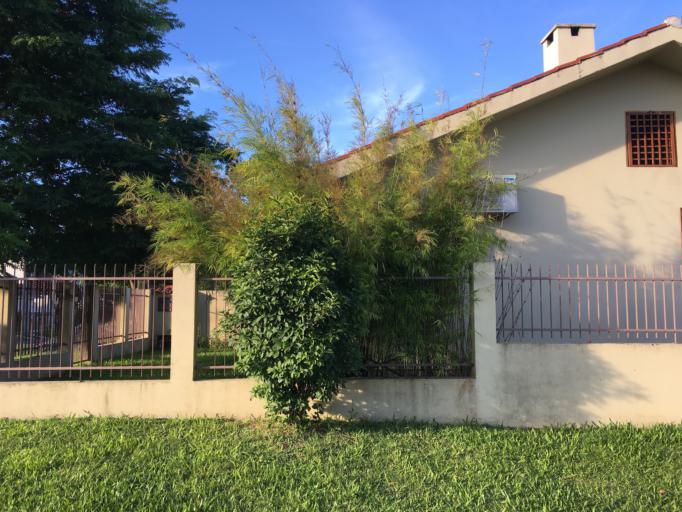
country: BR
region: Rio Grande do Sul
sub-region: Santa Maria
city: Santa Maria
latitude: -29.7010
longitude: -53.7091
